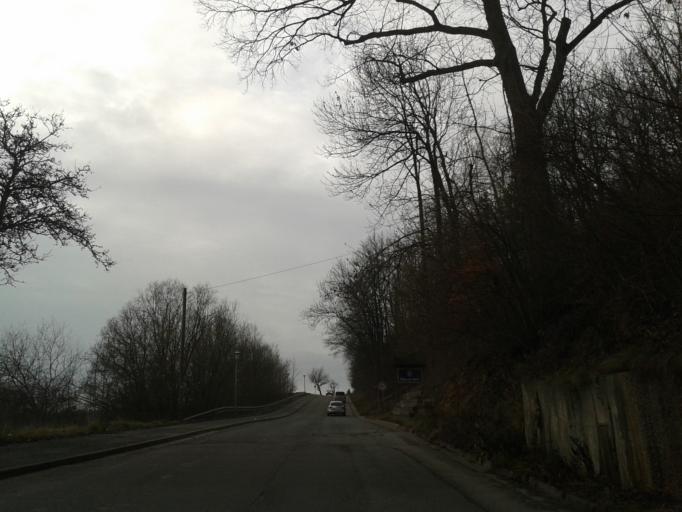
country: DE
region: Bavaria
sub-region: Upper Franconia
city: Coburg
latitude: 50.2599
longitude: 11.0054
